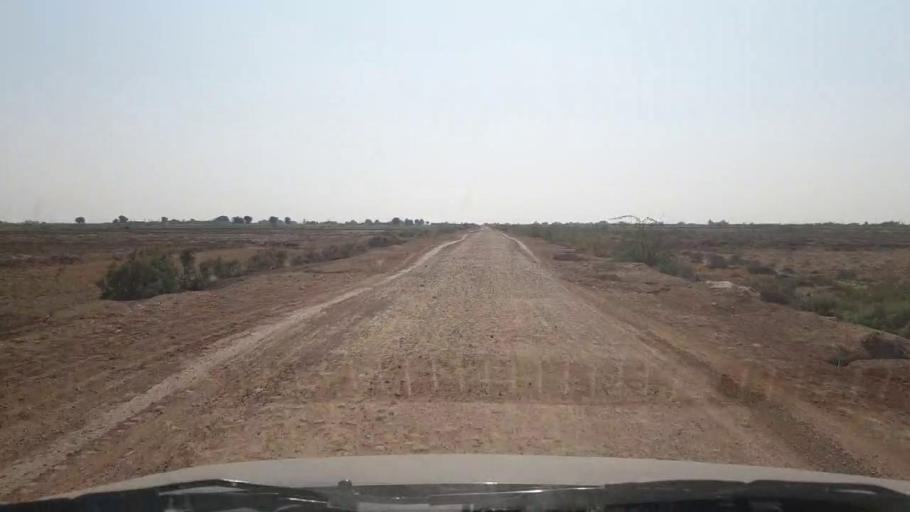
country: PK
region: Sindh
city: Samaro
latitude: 25.1932
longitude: 69.3424
